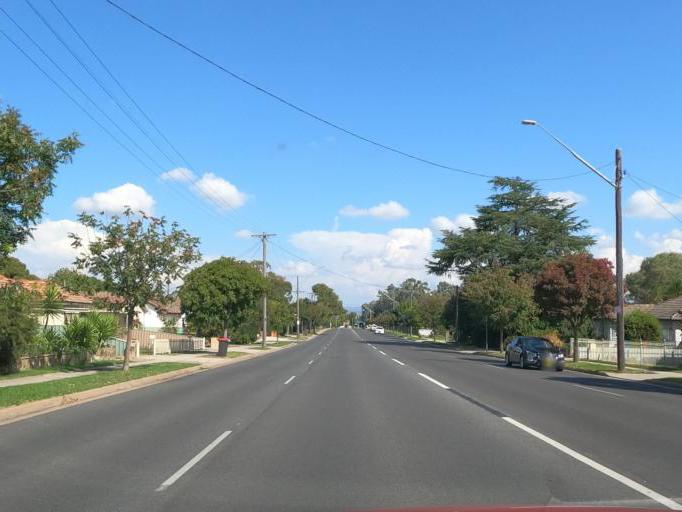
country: AU
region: New South Wales
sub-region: Albury Municipality
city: North Albury
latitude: -36.0587
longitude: 146.9269
